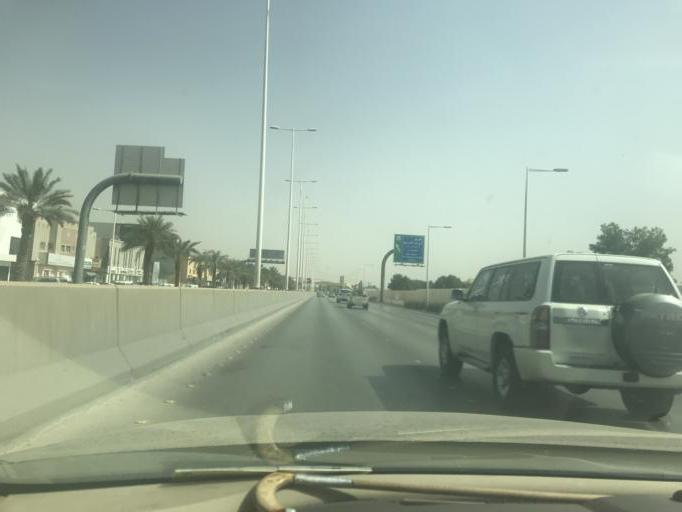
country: SA
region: Ar Riyad
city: Riyadh
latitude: 24.7367
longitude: 46.7069
